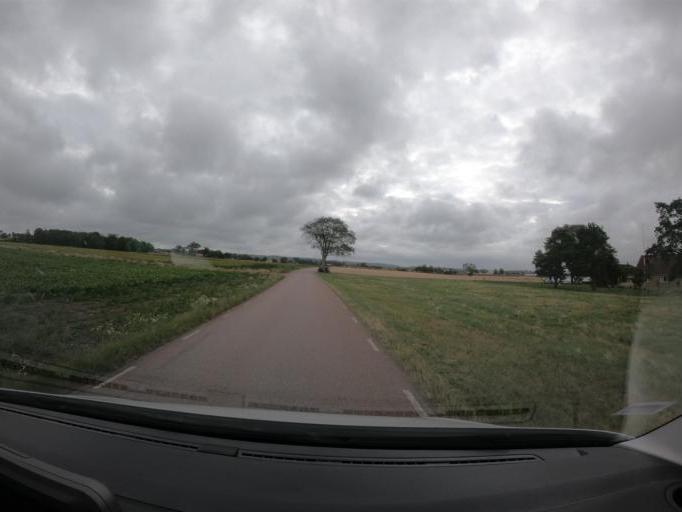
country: SE
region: Skane
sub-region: Angelholms Kommun
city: Vejbystrand
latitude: 56.3568
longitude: 12.7687
